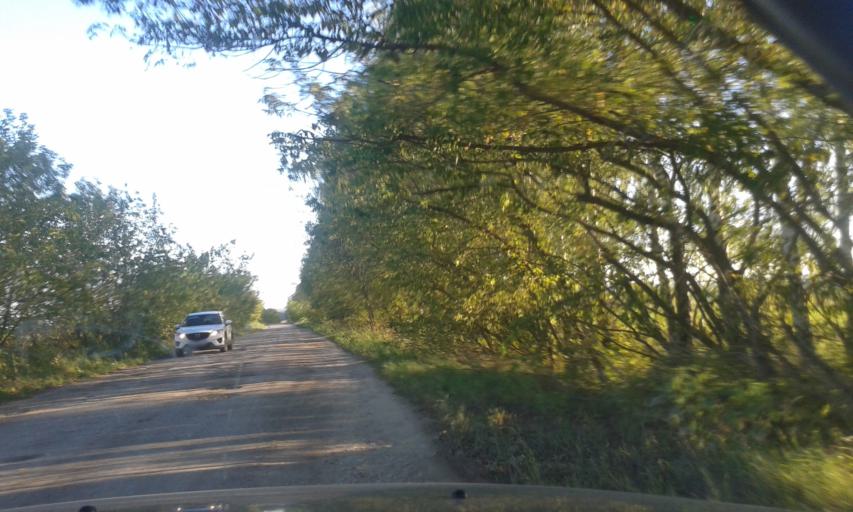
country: RU
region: Tula
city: Krapivna
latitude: 54.1298
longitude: 37.1567
